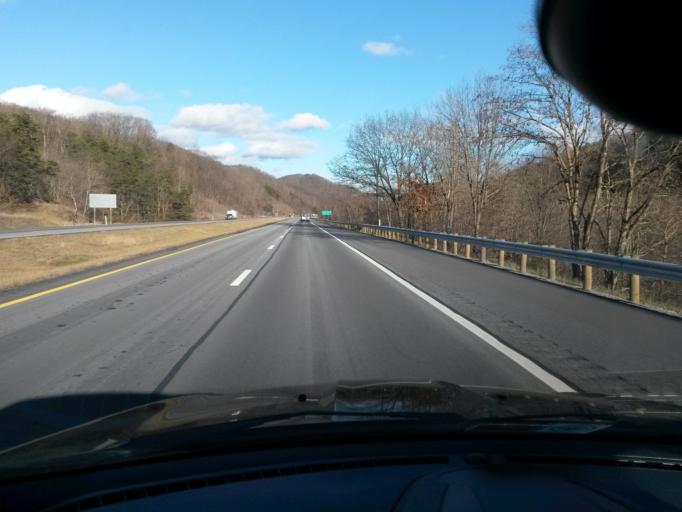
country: US
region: Virginia
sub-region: Giles County
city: Narrows
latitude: 37.3517
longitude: -80.9103
